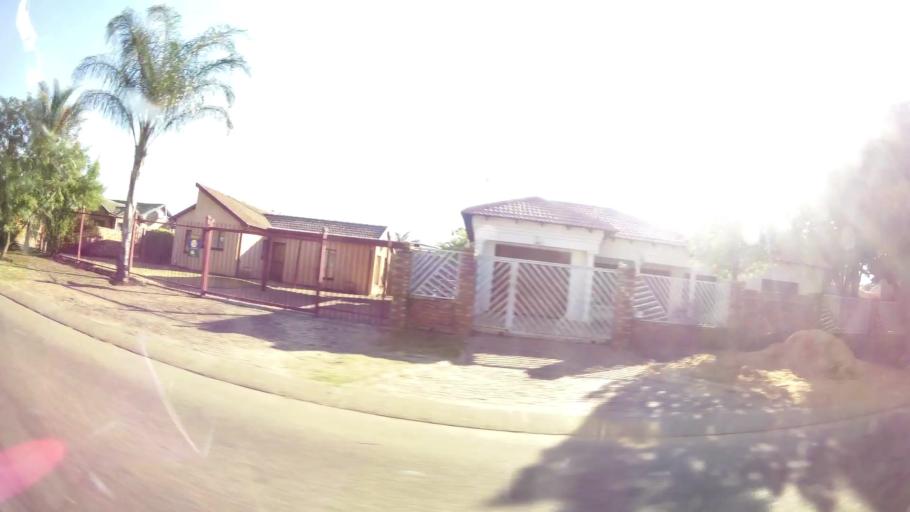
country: ZA
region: Gauteng
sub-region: City of Tshwane Metropolitan Municipality
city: Pretoria
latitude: -25.6717
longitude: 28.2194
